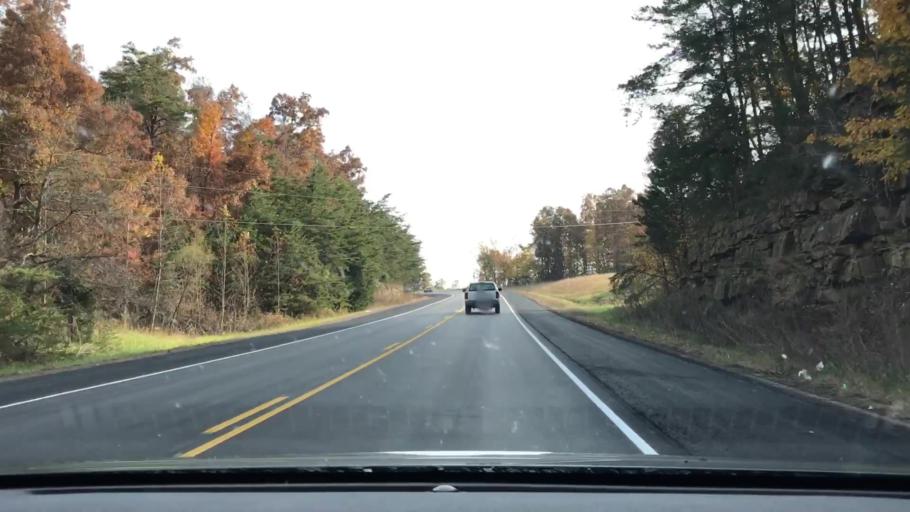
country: US
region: Tennessee
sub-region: Putnam County
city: Monterey
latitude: 36.1345
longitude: -85.1097
